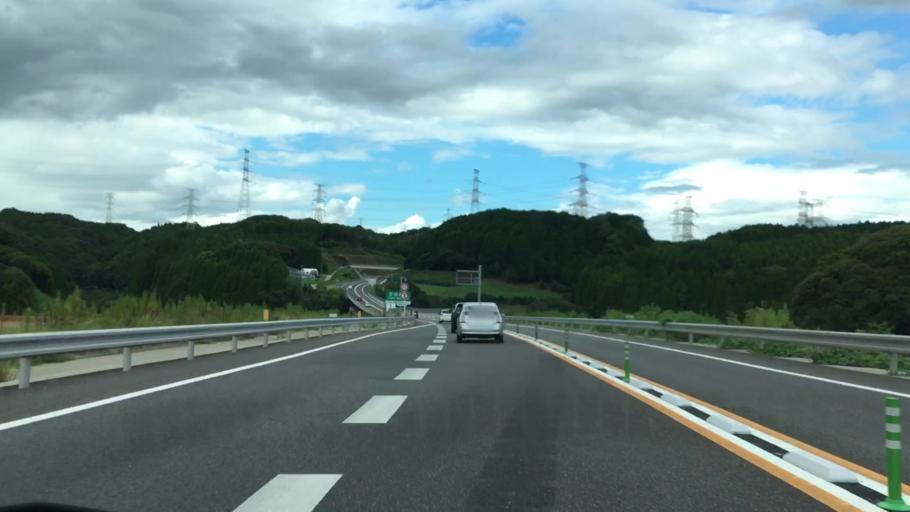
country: JP
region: Saga Prefecture
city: Imaricho-ko
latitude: 33.3461
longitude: 129.9246
